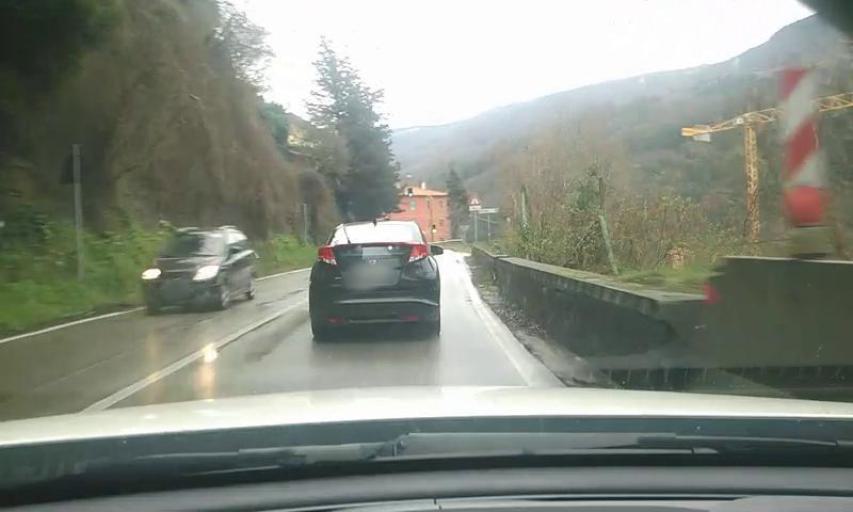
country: IT
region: Tuscany
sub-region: Provincia di Prato
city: Vaiano
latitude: 43.9310
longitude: 11.1264
